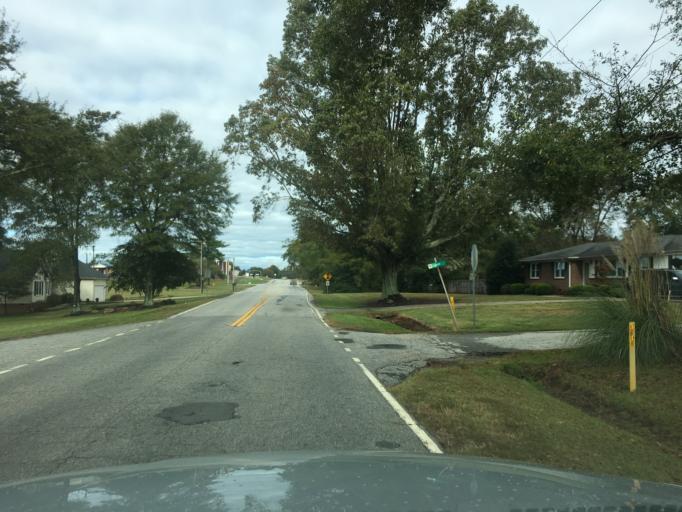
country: US
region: South Carolina
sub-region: Greenville County
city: Greer
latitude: 34.9704
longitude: -82.1976
